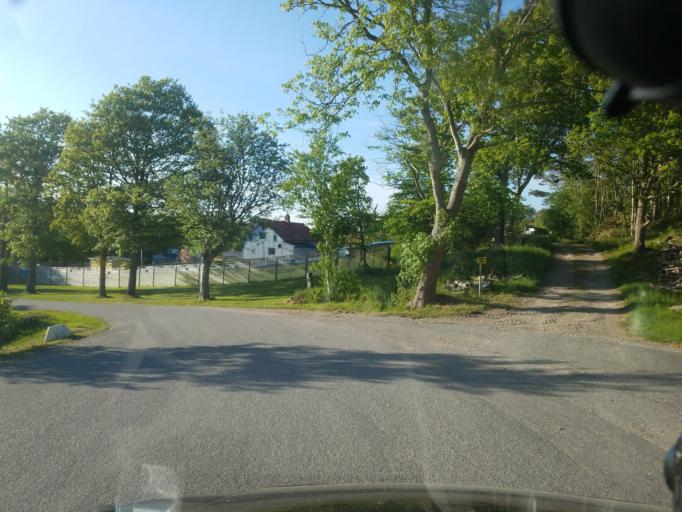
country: SE
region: Vaestra Goetaland
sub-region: Lysekils Kommun
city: Lysekil
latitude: 58.3055
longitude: 11.4609
